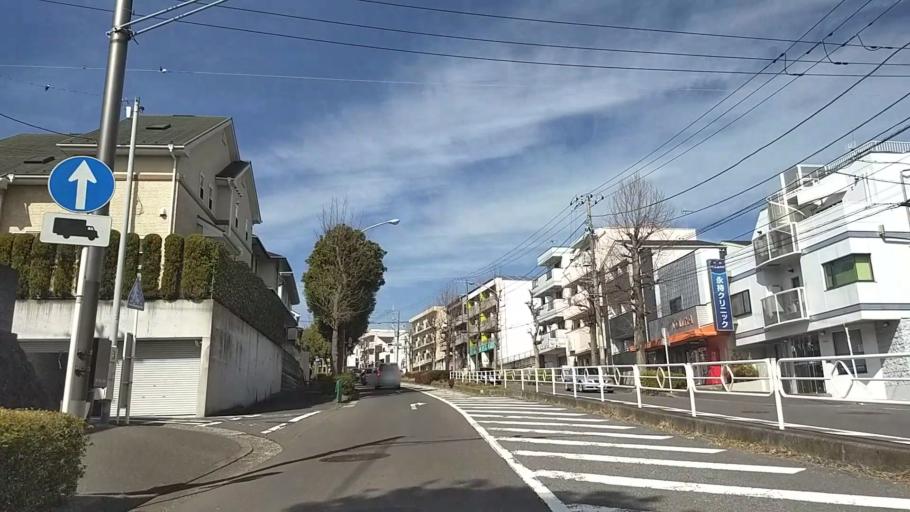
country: JP
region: Kanagawa
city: Kamakura
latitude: 35.3762
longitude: 139.5666
